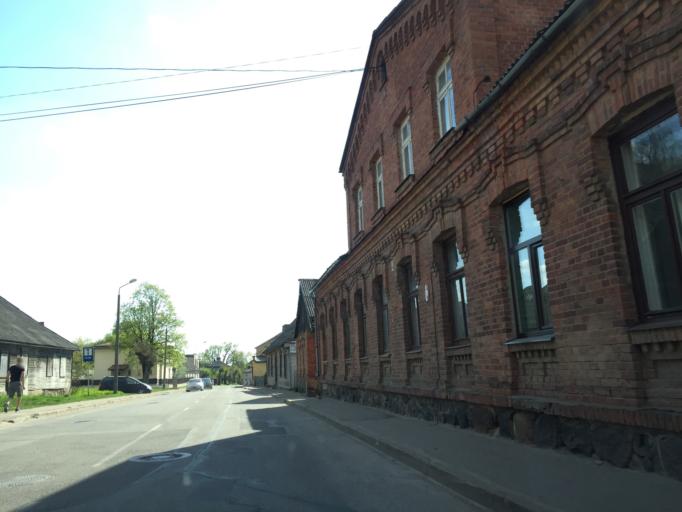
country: LV
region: Limbazu Rajons
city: Limbazi
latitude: 57.5134
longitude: 24.7096
